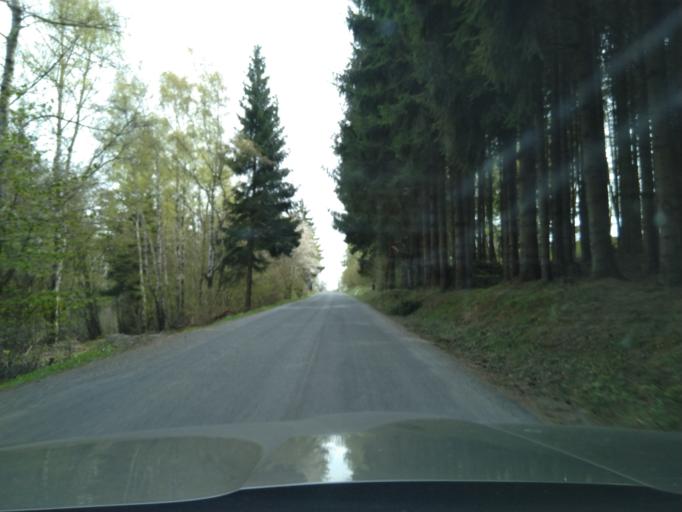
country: CZ
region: Jihocesky
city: Vacov
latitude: 49.1761
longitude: 13.6712
